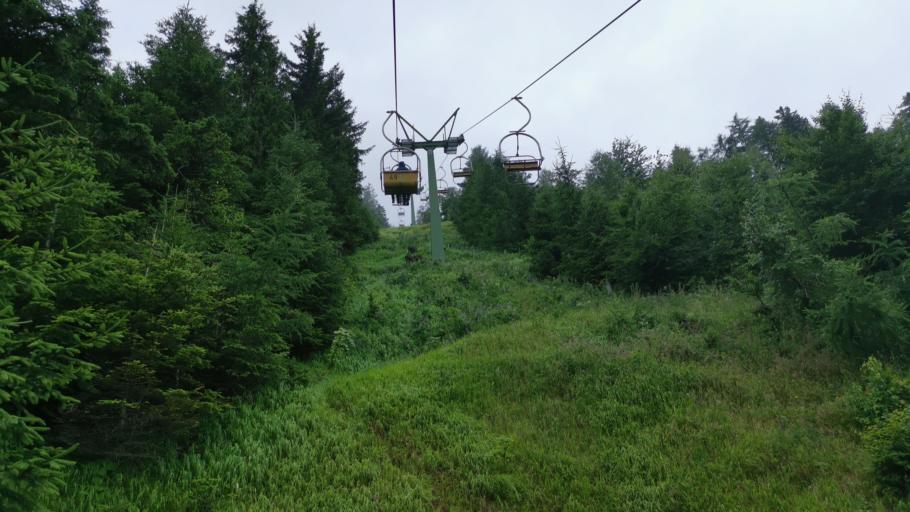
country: AT
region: Tyrol
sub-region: Politischer Bezirk Lienz
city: Leisach
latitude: 46.8223
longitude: 12.7346
